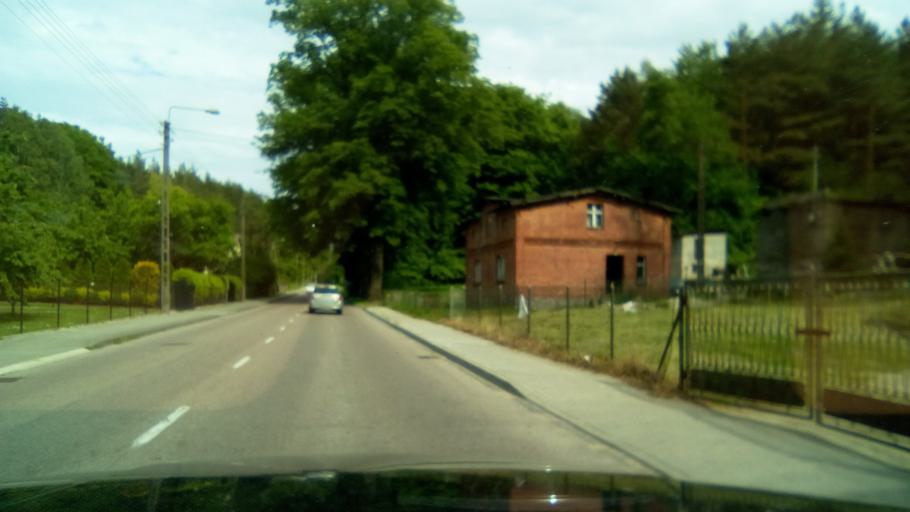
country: PL
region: Pomeranian Voivodeship
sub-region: Powiat pucki
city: Krokowa
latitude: 54.7856
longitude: 18.0931
